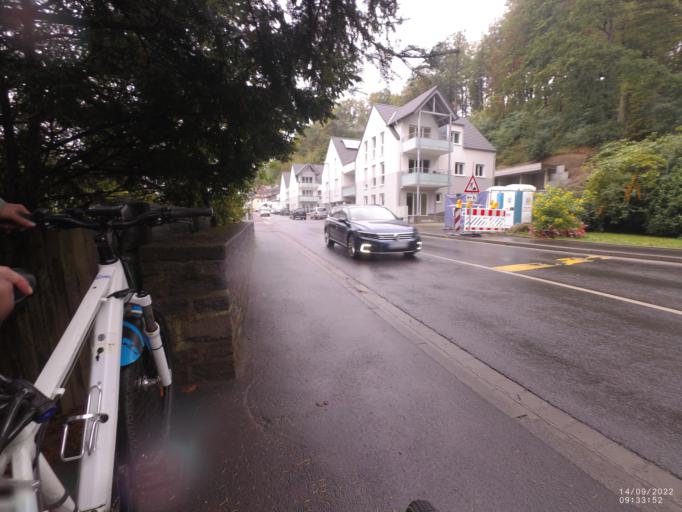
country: DE
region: Bavaria
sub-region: Regierungsbezirk Unterfranken
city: Glattbach
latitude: 49.9989
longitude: 9.1538
